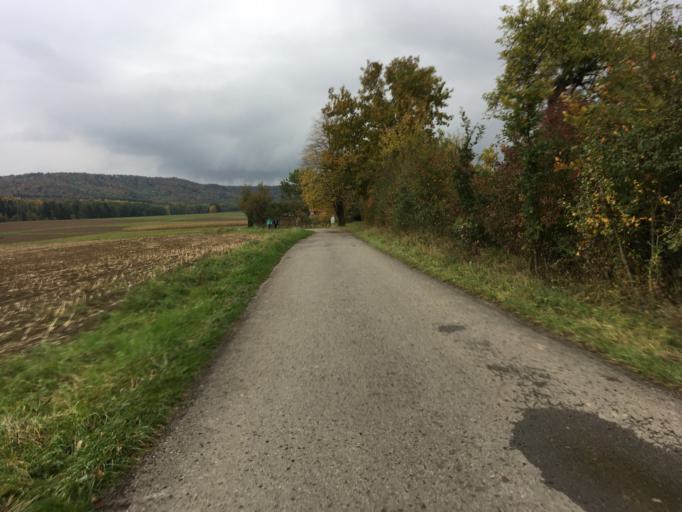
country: DE
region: Baden-Wuerttemberg
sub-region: Tuebingen Region
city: Gomaringen
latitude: 48.4429
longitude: 9.0849
